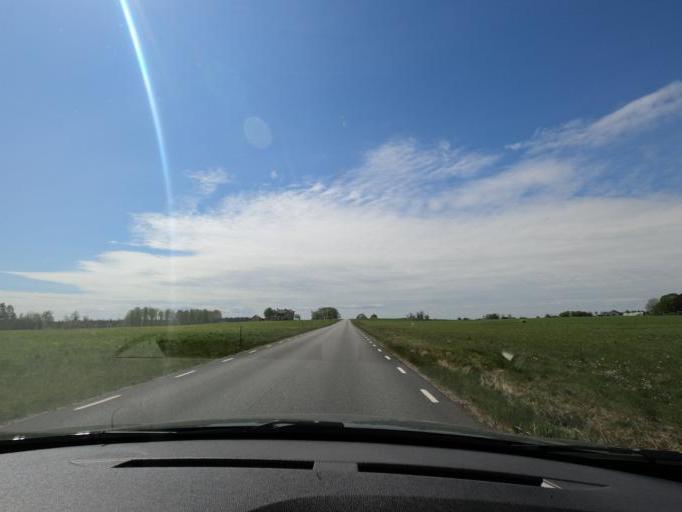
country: SE
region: Joenkoeping
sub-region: Varnamo Kommun
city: Bredaryd
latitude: 57.1471
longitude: 13.7235
